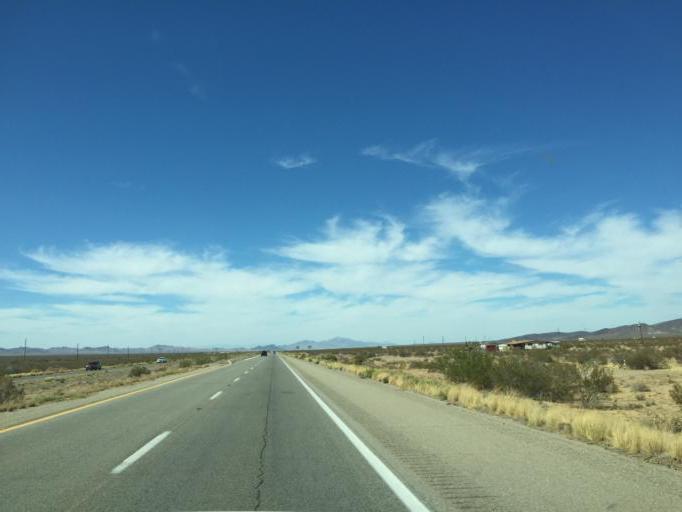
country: US
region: Arizona
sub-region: Mohave County
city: Dolan Springs
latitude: 35.5905
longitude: -114.3944
